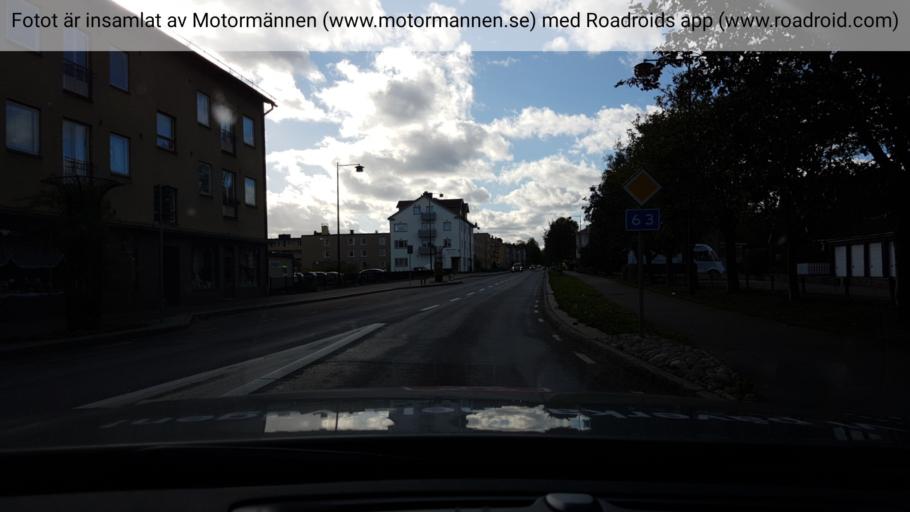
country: SE
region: Vaermland
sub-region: Filipstads Kommun
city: Filipstad
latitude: 59.7140
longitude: 14.1692
